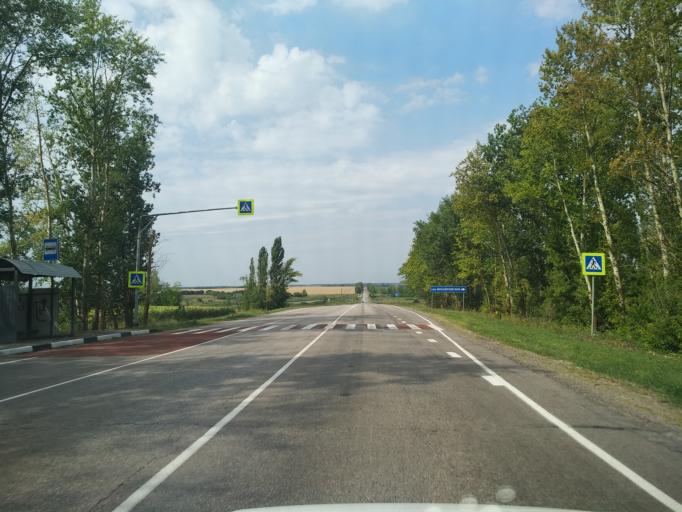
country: RU
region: Voronezj
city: Verkhnyaya Khava
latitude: 51.7041
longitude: 39.9788
